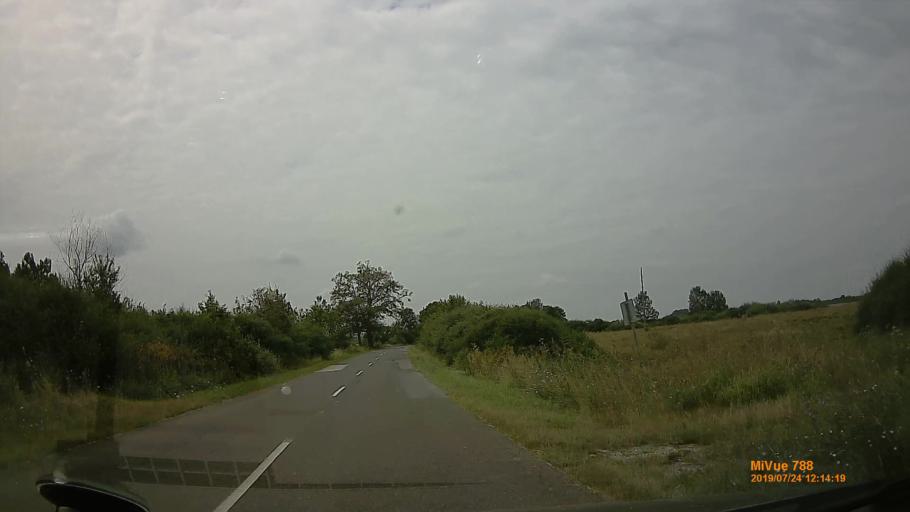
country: HU
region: Szabolcs-Szatmar-Bereg
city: Vasarosnameny
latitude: 48.1900
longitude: 22.3541
